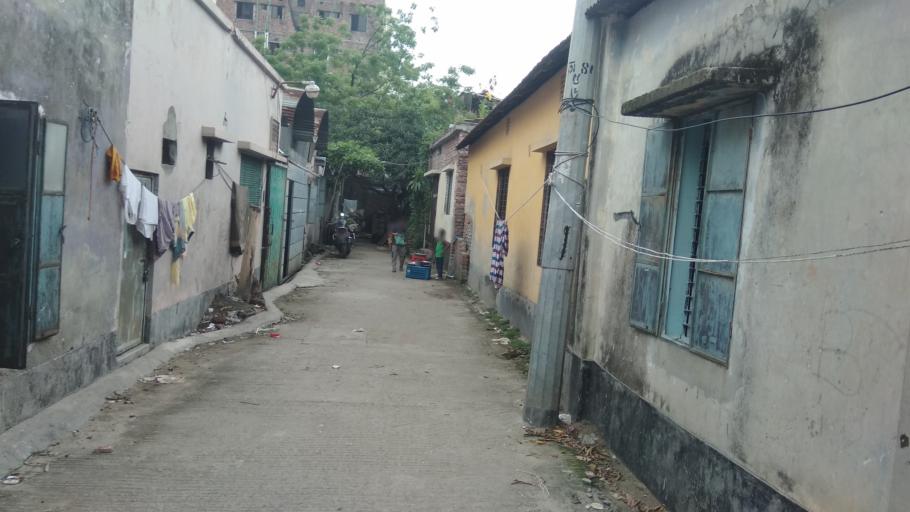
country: BD
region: Dhaka
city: Azimpur
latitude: 23.7989
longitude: 90.3758
